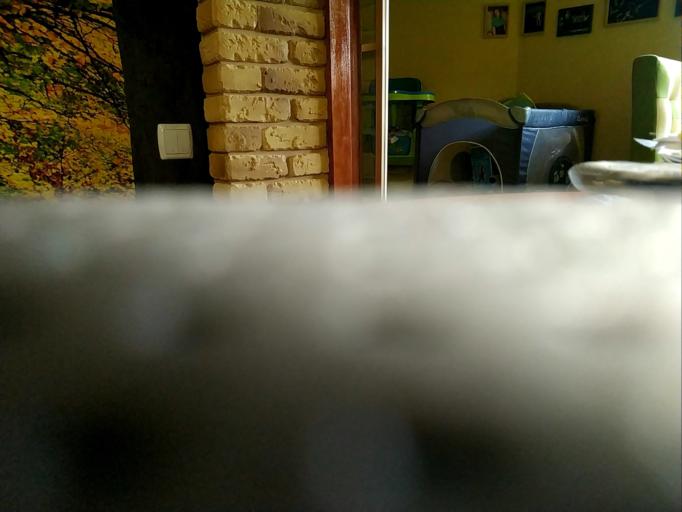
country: RU
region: Kaluga
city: Seredeyskiy
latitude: 53.8919
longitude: 35.3585
